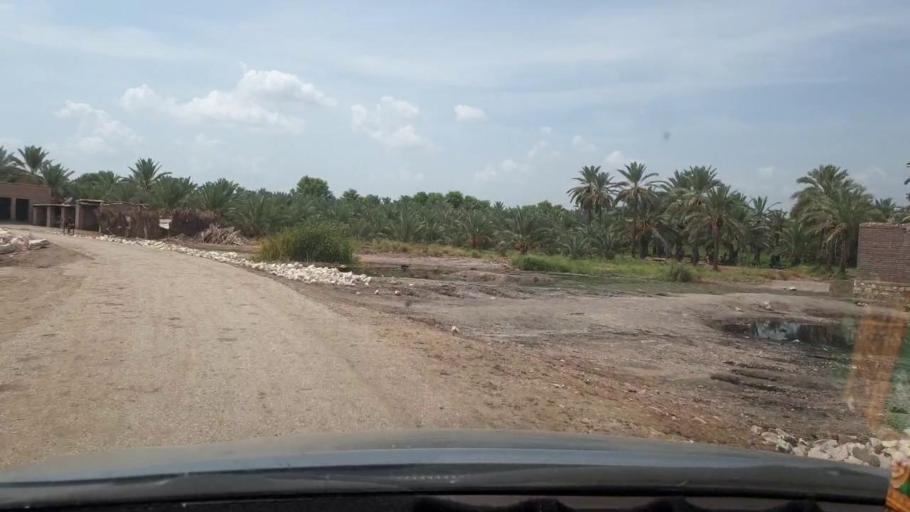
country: PK
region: Sindh
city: Khairpur
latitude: 27.4600
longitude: 68.8230
